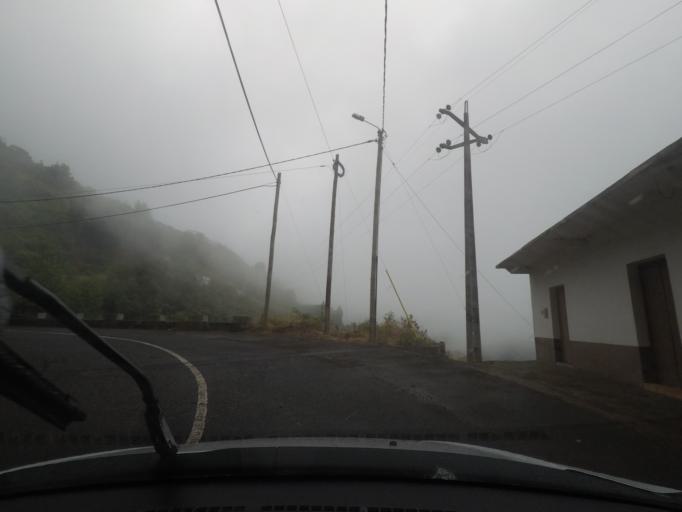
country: PT
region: Madeira
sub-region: Santana
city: Santana
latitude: 32.7762
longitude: -16.8690
